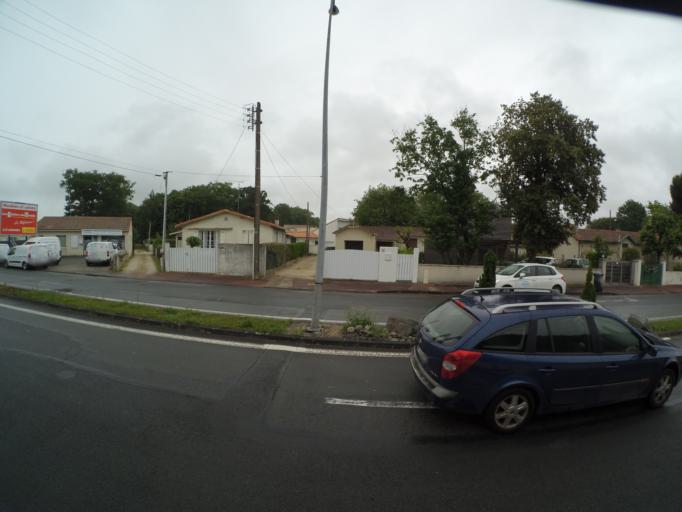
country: FR
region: Poitou-Charentes
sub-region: Departement de la Charente-Maritime
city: Saint-Georges-de-Didonne
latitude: 45.6149
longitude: -1.0012
